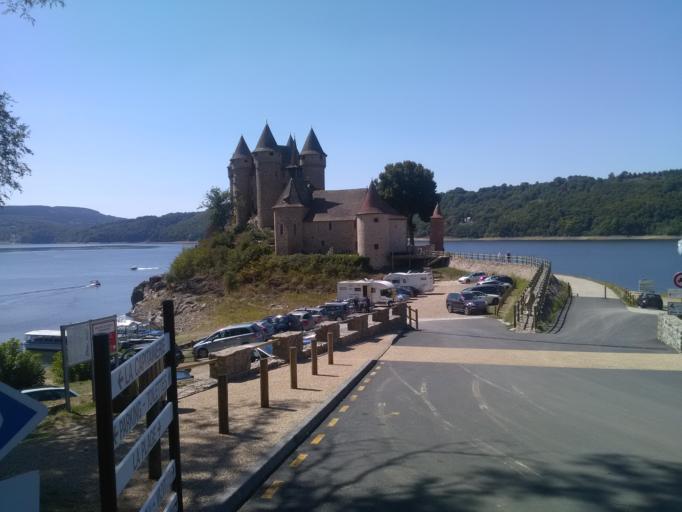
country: FR
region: Auvergne
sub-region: Departement du Cantal
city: Lanobre
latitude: 45.4434
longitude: 2.5069
